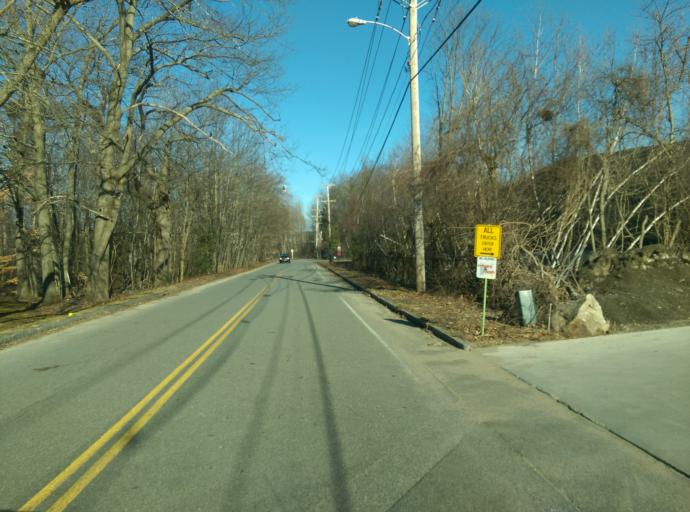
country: US
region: Massachusetts
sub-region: Essex County
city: Haverhill
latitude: 42.7630
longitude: -71.1128
